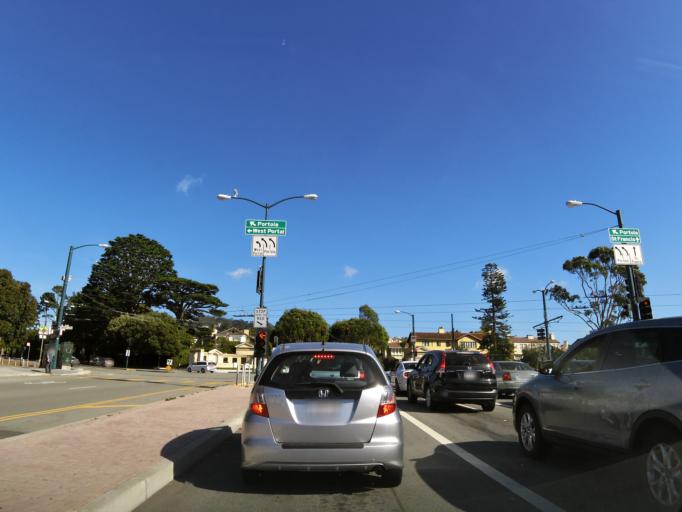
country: US
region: California
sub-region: San Mateo County
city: Daly City
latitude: 37.7348
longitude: -122.4721
